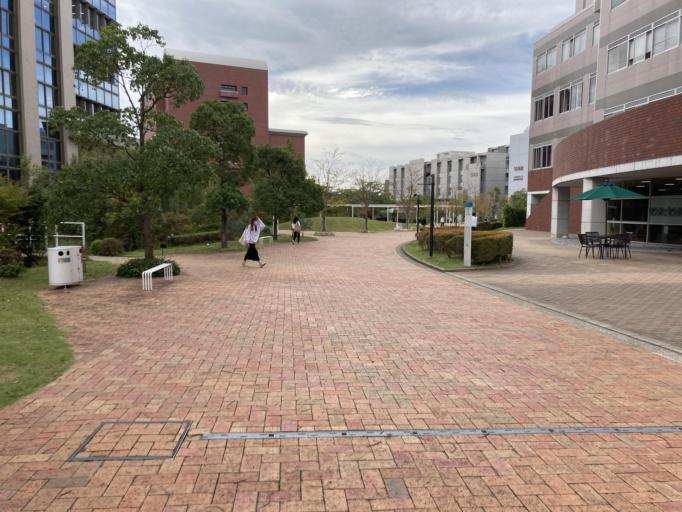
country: JP
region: Fukuoka
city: Shingu
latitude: 33.6713
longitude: 130.4453
